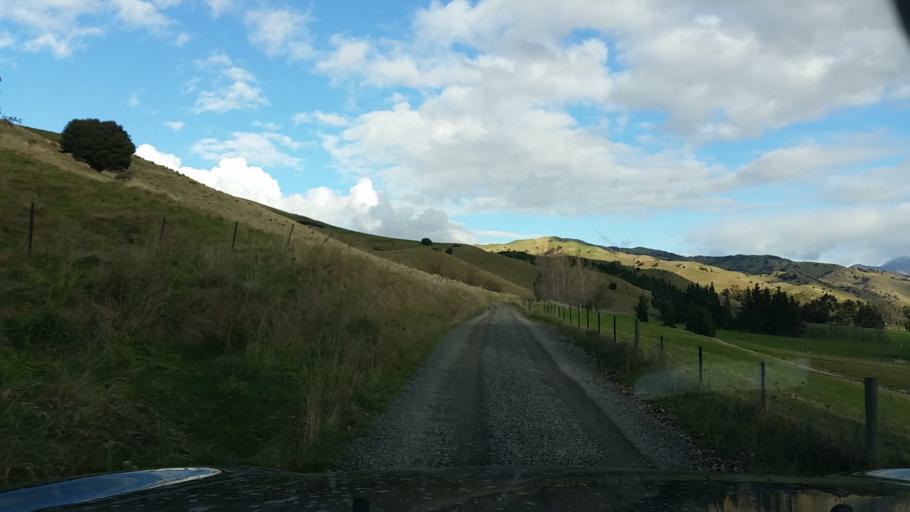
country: NZ
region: Marlborough
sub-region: Marlborough District
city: Blenheim
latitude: -41.7679
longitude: 173.8578
